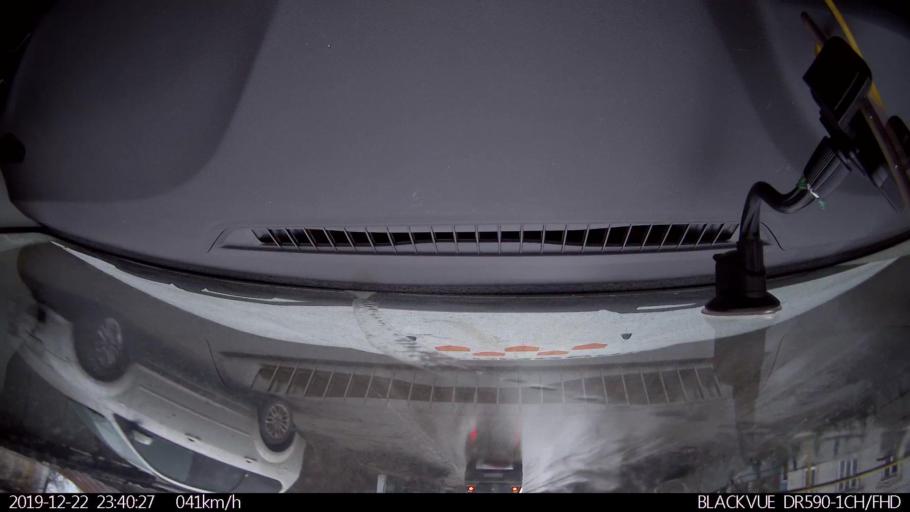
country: RU
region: Nizjnij Novgorod
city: Nizhniy Novgorod
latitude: 56.2789
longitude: 43.9045
